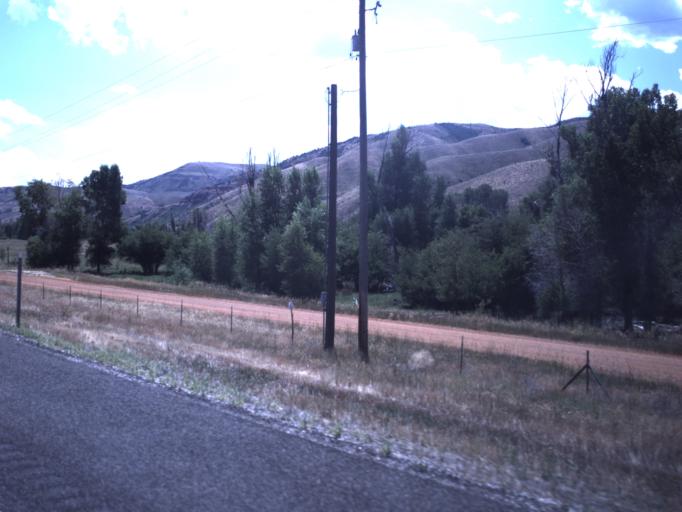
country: US
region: Utah
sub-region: Summit County
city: Coalville
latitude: 40.9941
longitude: -111.4620
